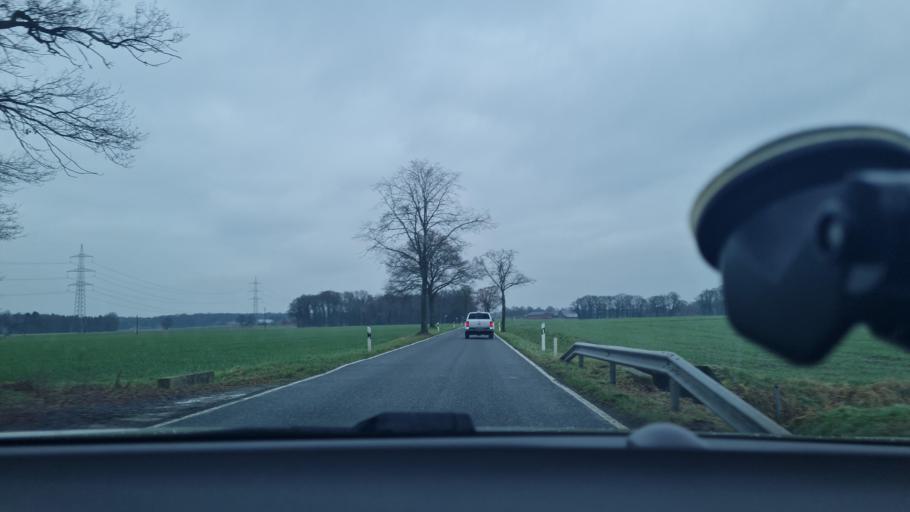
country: DE
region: North Rhine-Westphalia
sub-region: Regierungsbezirk Dusseldorf
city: Hunxe
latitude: 51.7344
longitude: 6.7691
